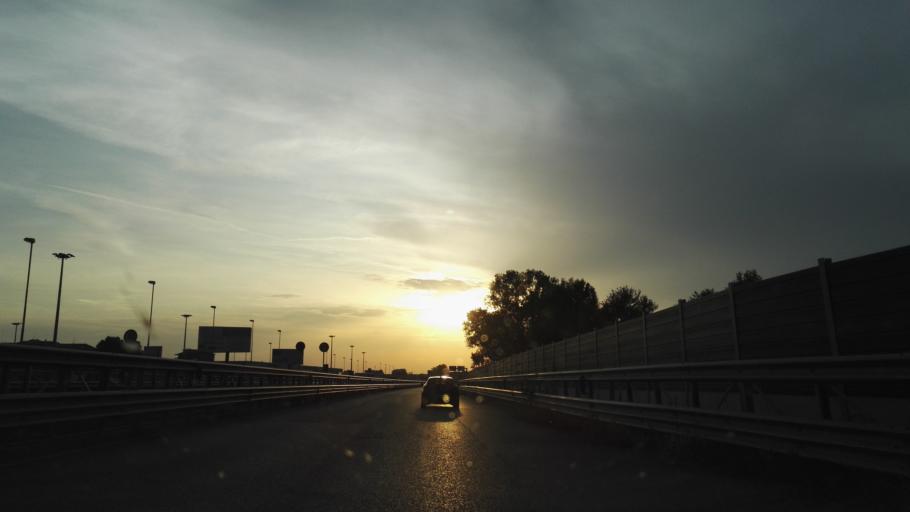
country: IT
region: Lombardy
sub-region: Citta metropolitana di Milano
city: Mombretto
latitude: 45.4295
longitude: 9.3704
